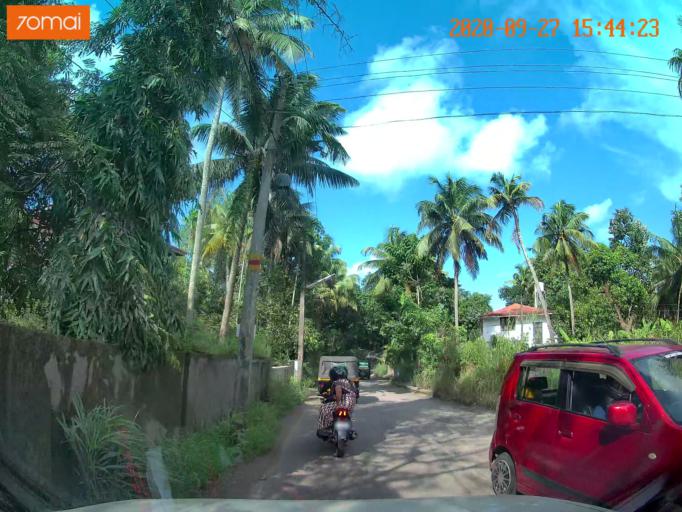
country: IN
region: Kerala
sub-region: Thrissur District
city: Thanniyam
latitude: 10.4764
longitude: 76.1128
